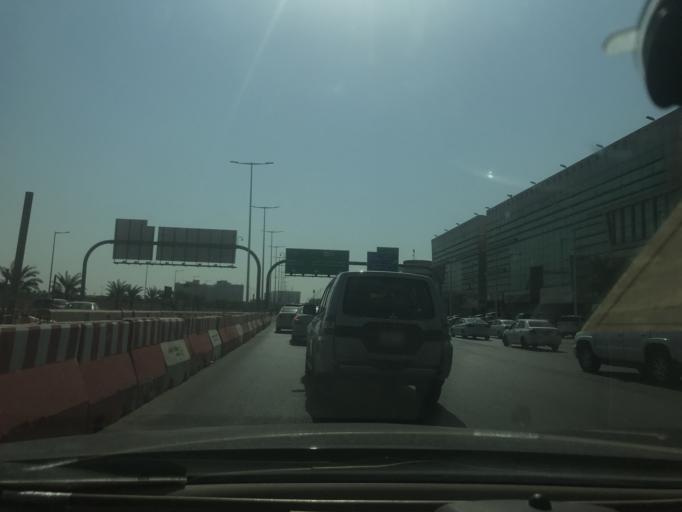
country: SA
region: Ar Riyad
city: Riyadh
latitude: 24.6987
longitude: 46.7230
